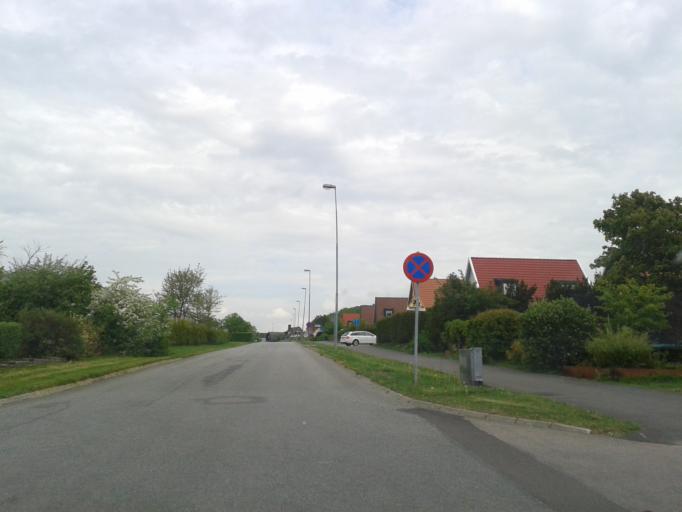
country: SE
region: Vaestra Goetaland
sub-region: Kungalvs Kommun
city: Kungalv
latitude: 57.8812
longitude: 11.9607
